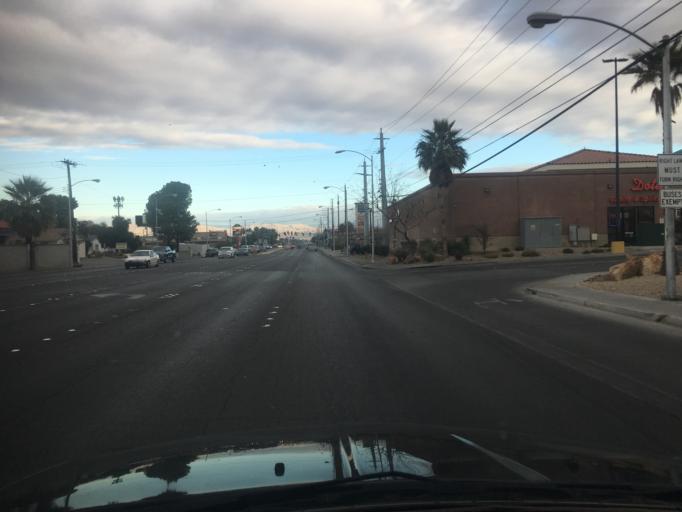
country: US
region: Nevada
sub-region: Clark County
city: Whitney
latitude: 36.1105
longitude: -115.0644
